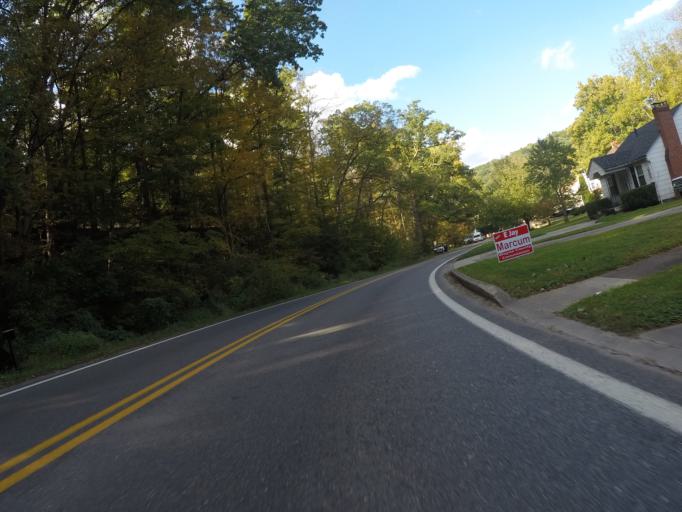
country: US
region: Ohio
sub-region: Lawrence County
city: Burlington
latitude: 38.3893
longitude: -82.5121
